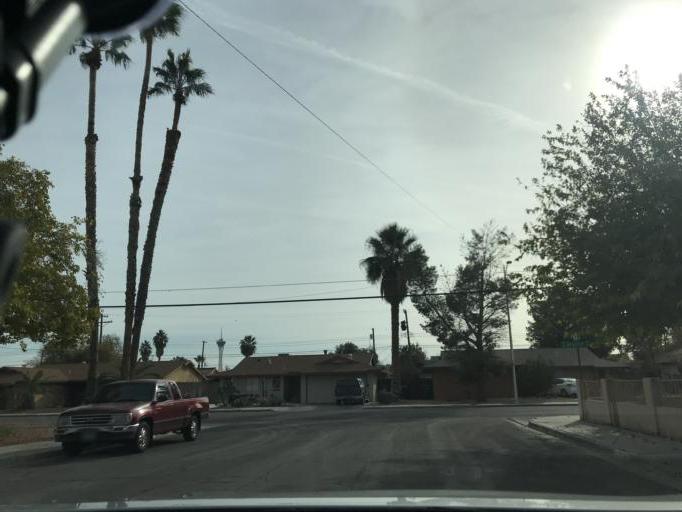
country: US
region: Nevada
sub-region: Clark County
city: Las Vegas
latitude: 36.1744
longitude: -115.1678
